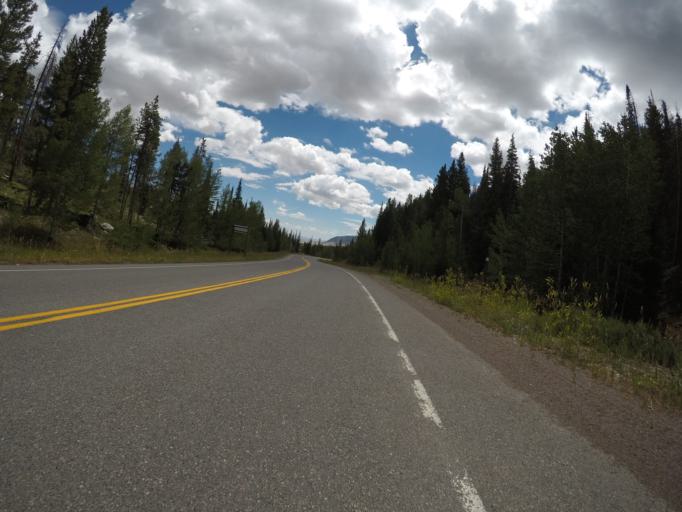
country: US
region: Wyoming
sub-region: Albany County
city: Laramie
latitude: 41.3159
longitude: -106.1595
